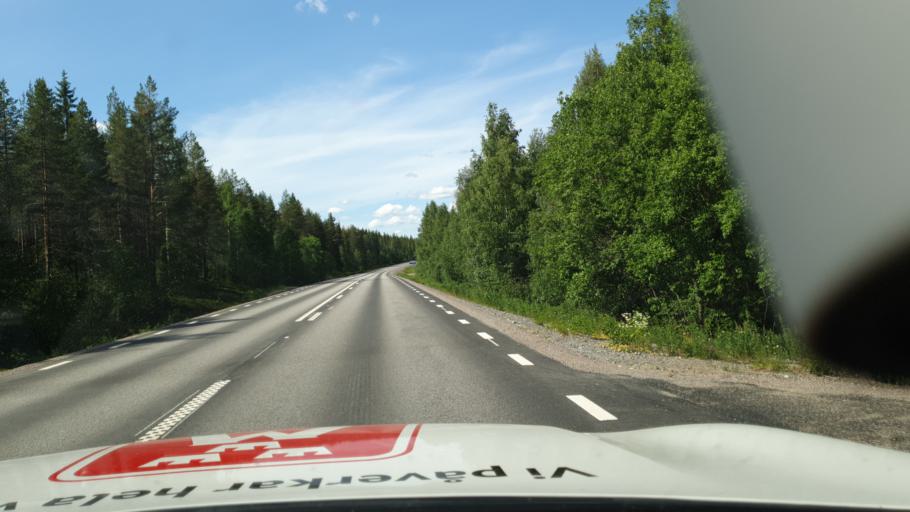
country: SE
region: Vaesterbotten
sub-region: Skelleftea Kommun
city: Boliden
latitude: 64.8845
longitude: 20.3860
